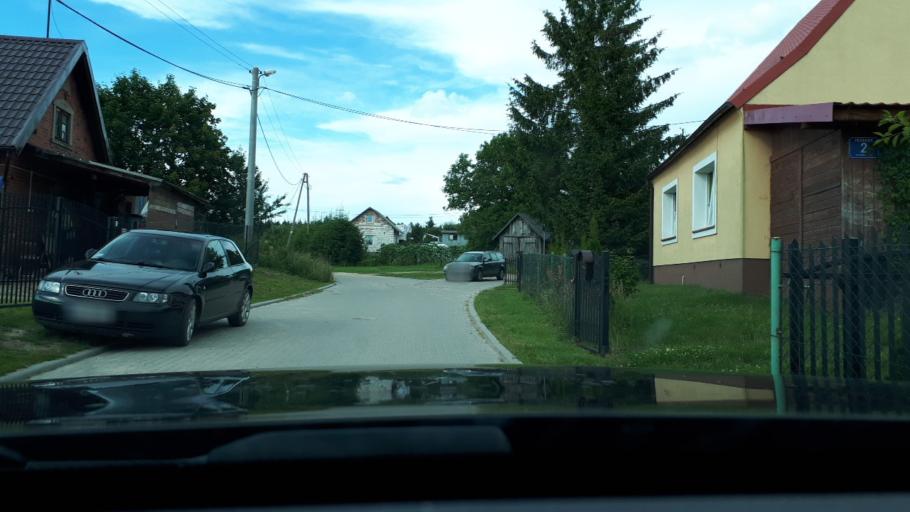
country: PL
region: Warmian-Masurian Voivodeship
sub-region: Powiat ostrodzki
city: Ostroda
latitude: 53.6785
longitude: 20.0437
